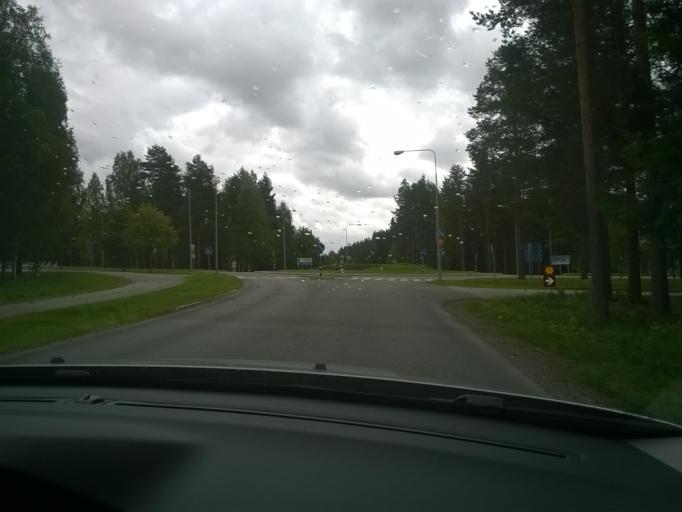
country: FI
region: Kainuu
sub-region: Kehys-Kainuu
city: Kuhmo
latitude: 64.1229
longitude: 29.5070
